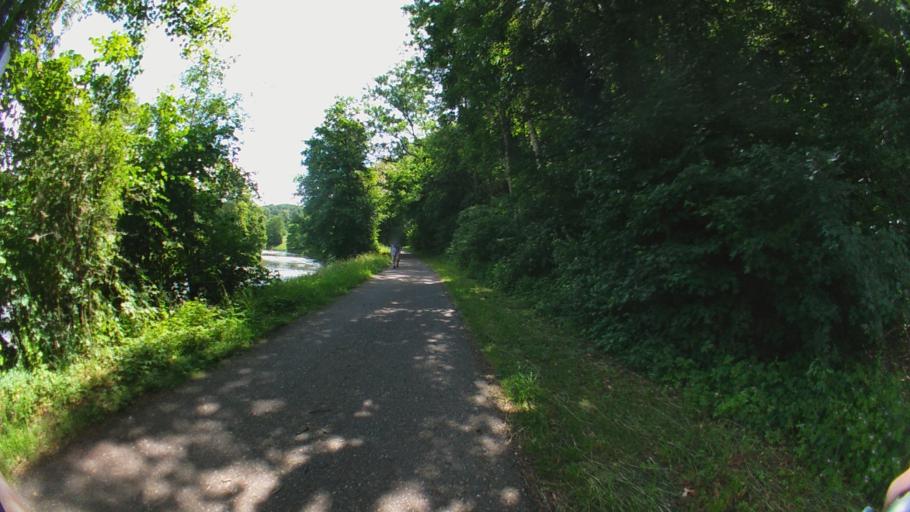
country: CH
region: Zurich
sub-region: Bezirk Buelach
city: Glattfelden
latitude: 47.5496
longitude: 8.5168
